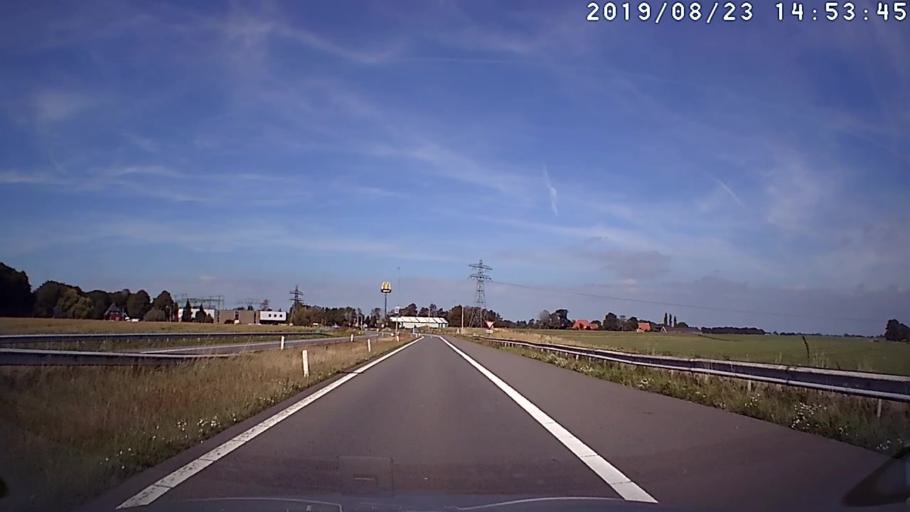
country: NL
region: Friesland
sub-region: Gemeente Lemsterland
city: Lemmer
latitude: 52.8464
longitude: 5.7253
